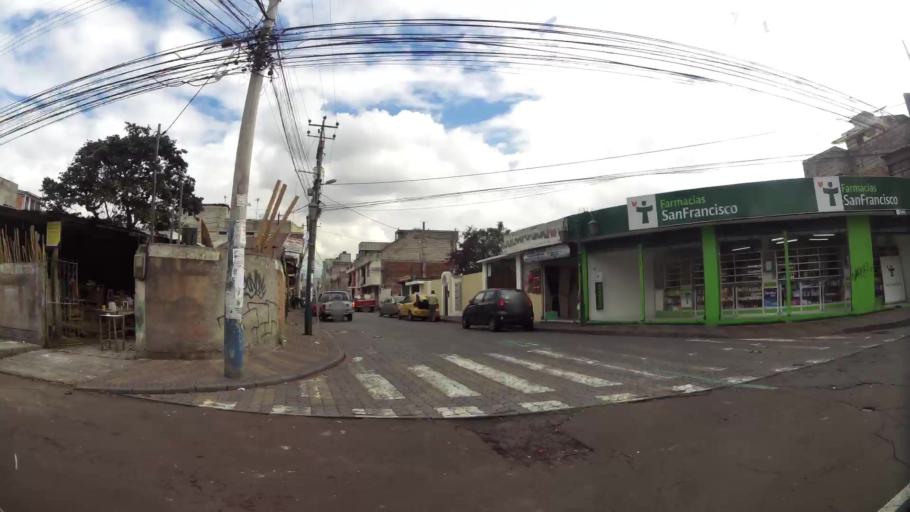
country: EC
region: Pichincha
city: Sangolqui
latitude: -0.3251
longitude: -78.4487
